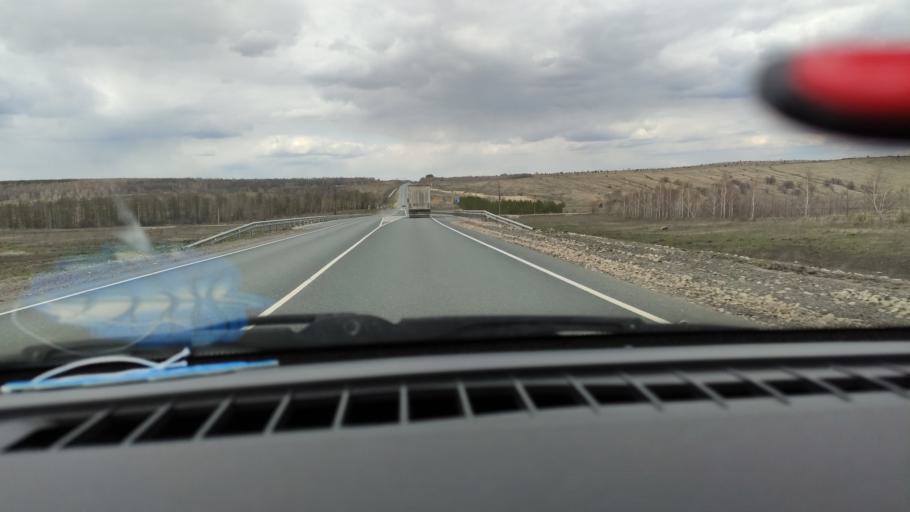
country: RU
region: Saratov
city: Shikhany
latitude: 52.1371
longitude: 47.2158
